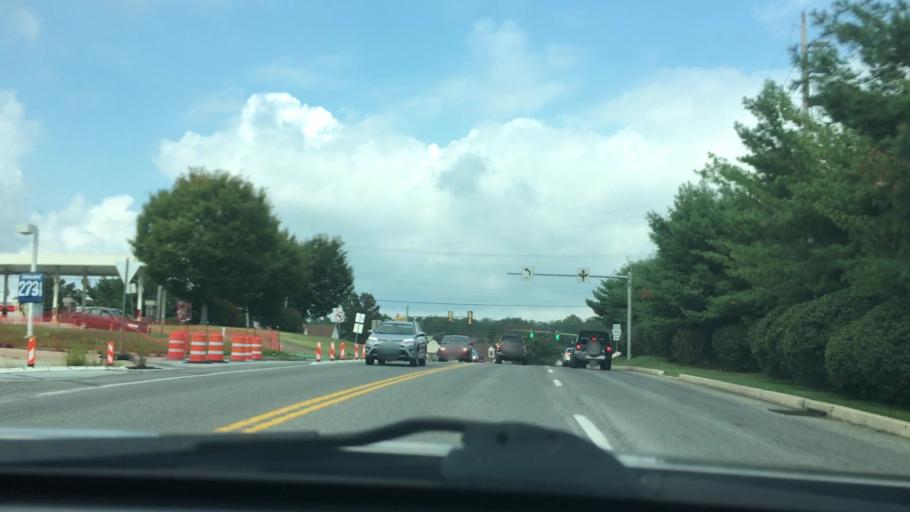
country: US
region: Pennsylvania
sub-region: Chester County
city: Malvern
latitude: 39.9653
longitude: -75.5206
